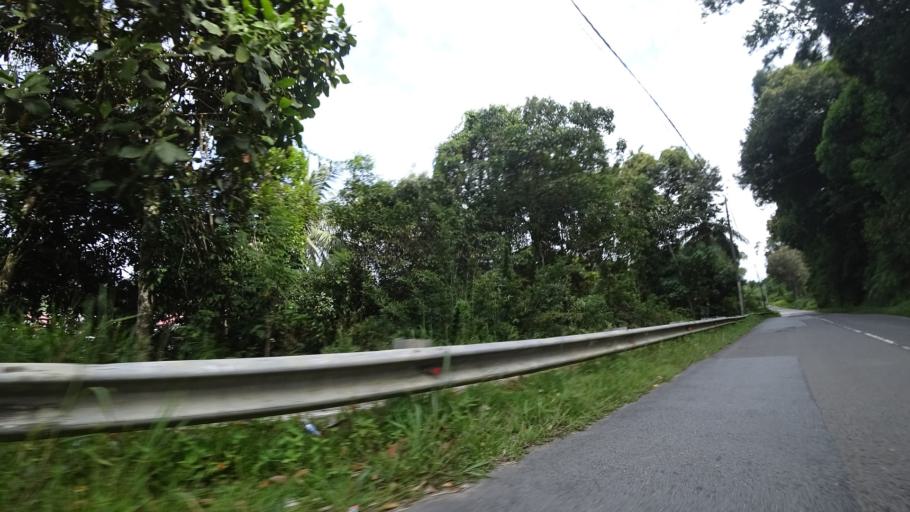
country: BN
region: Brunei and Muara
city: Bandar Seri Begawan
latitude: 4.8591
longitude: 114.9524
